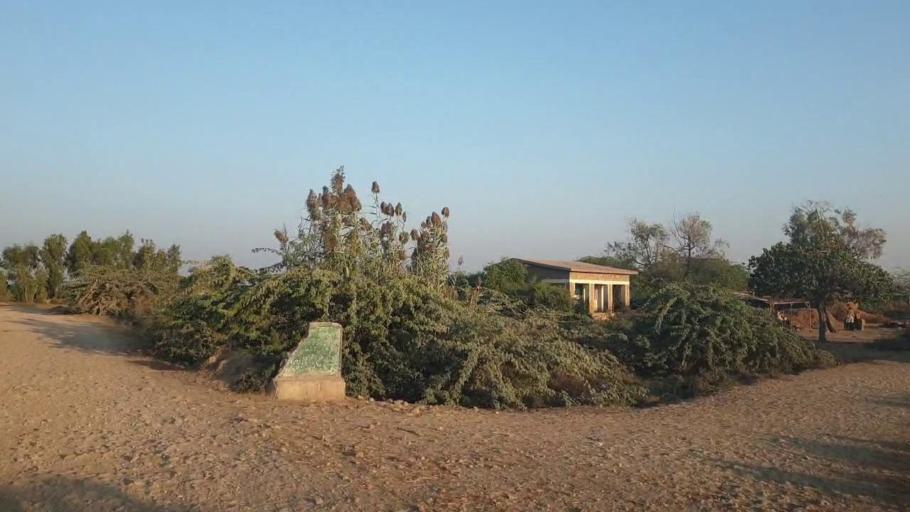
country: PK
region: Sindh
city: Mirpur Sakro
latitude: 24.4602
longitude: 67.5985
